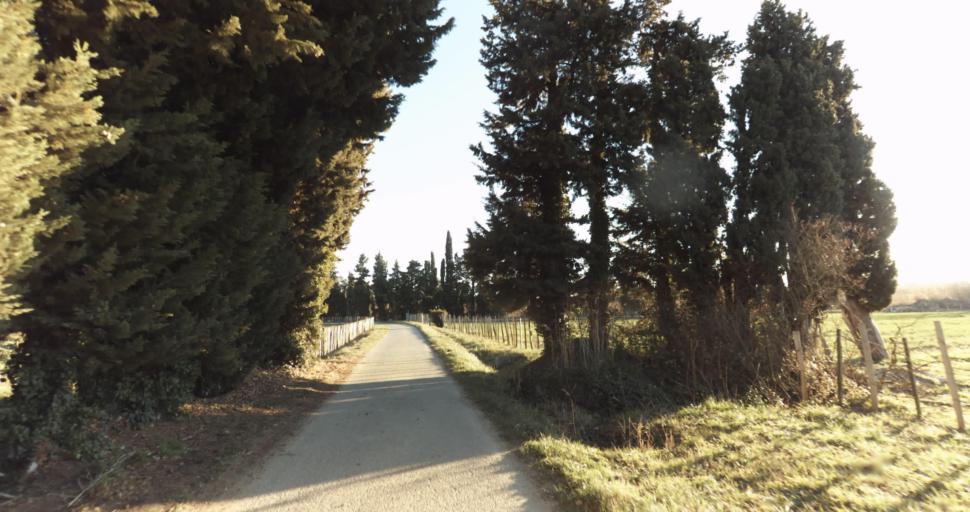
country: FR
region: Provence-Alpes-Cote d'Azur
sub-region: Departement des Bouches-du-Rhone
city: Barbentane
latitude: 43.9150
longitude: 4.7684
